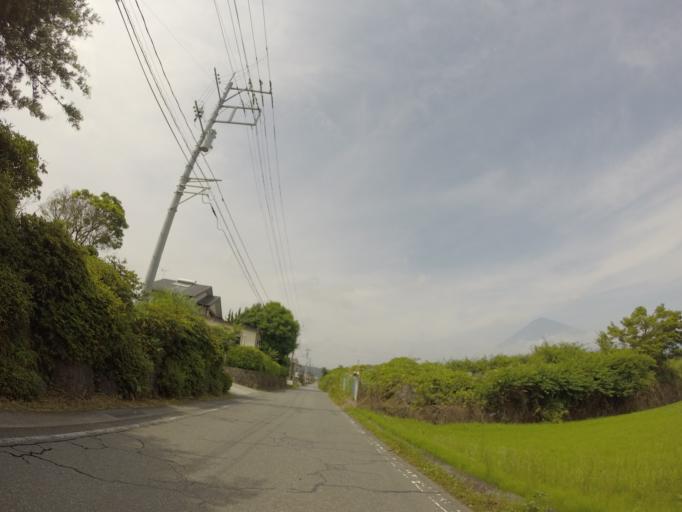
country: JP
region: Shizuoka
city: Fujinomiya
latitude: 35.2804
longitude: 138.5746
